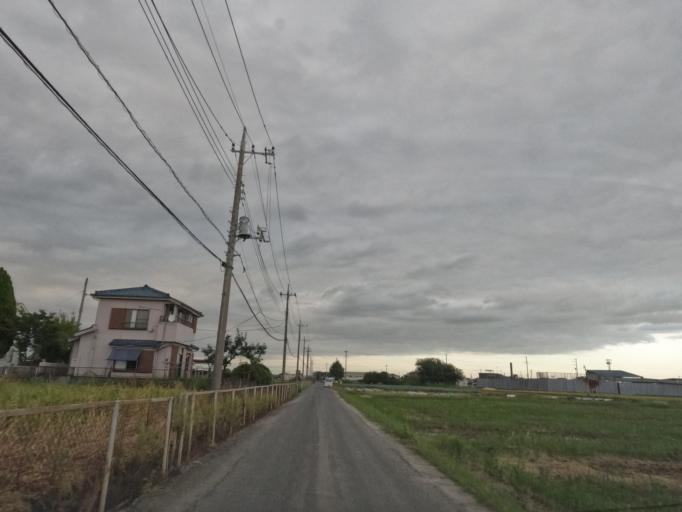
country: JP
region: Saitama
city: Koshigaya
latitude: 35.9003
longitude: 139.7567
